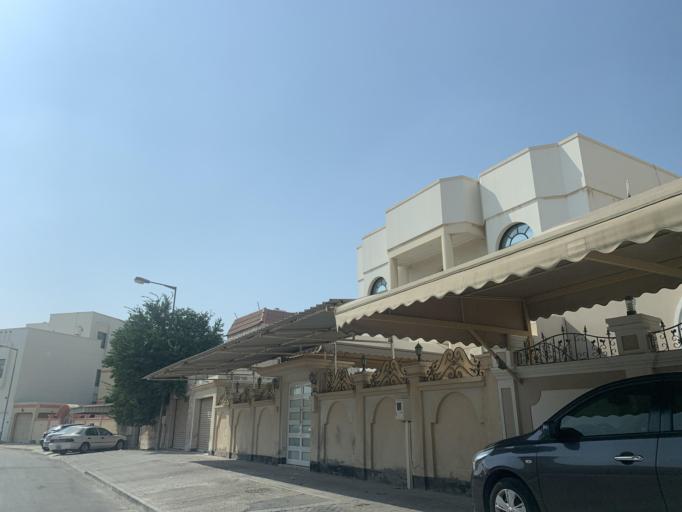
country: BH
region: Central Governorate
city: Madinat Hamad
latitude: 26.1316
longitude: 50.4936
